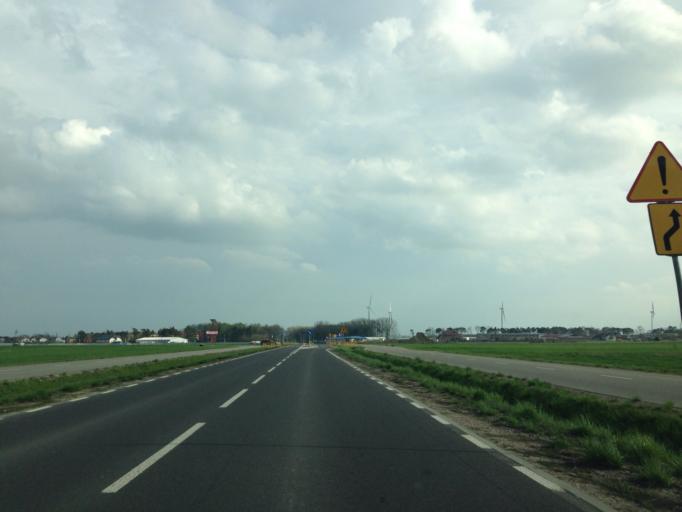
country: PL
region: Masovian Voivodeship
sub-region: Powiat zurominski
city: Zuromin
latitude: 53.0676
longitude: 19.8920
